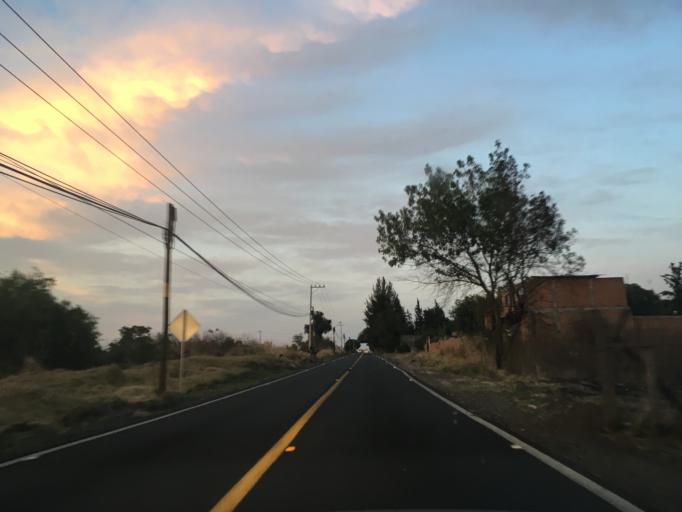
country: MX
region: Michoacan
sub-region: Morelia
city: Morelos
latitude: 19.6424
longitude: -101.2554
